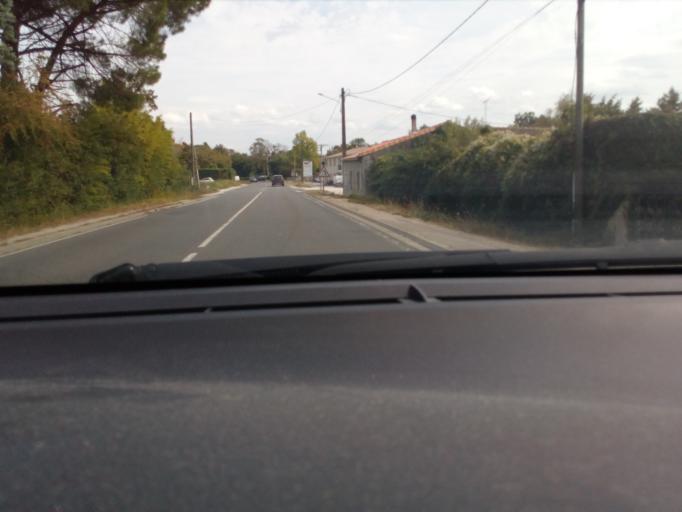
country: FR
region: Poitou-Charentes
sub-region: Departement de la Charente
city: Fleac
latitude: 45.6728
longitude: 0.0984
